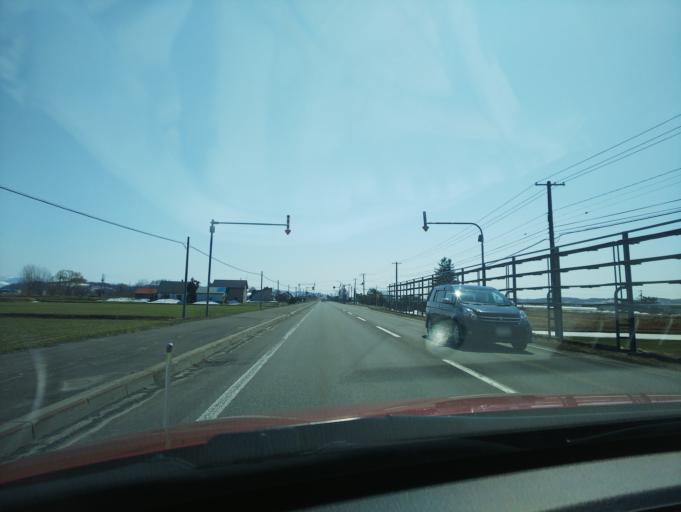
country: JP
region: Hokkaido
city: Nayoro
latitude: 44.2025
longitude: 142.3949
